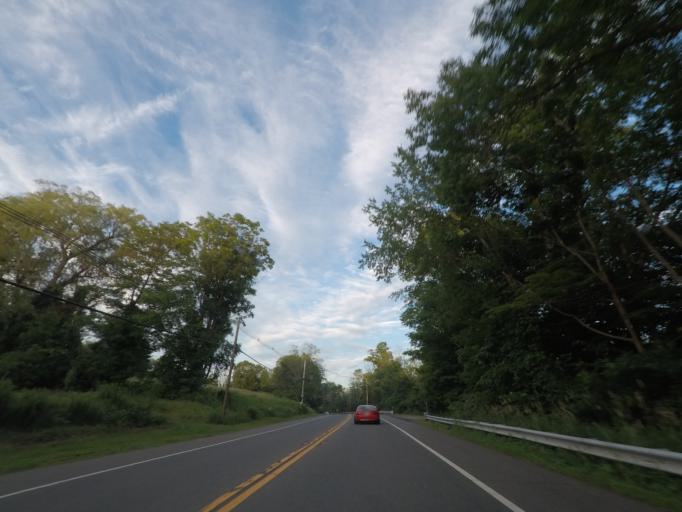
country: US
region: Massachusetts
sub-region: Worcester County
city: Warren
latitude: 42.2159
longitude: -72.2181
